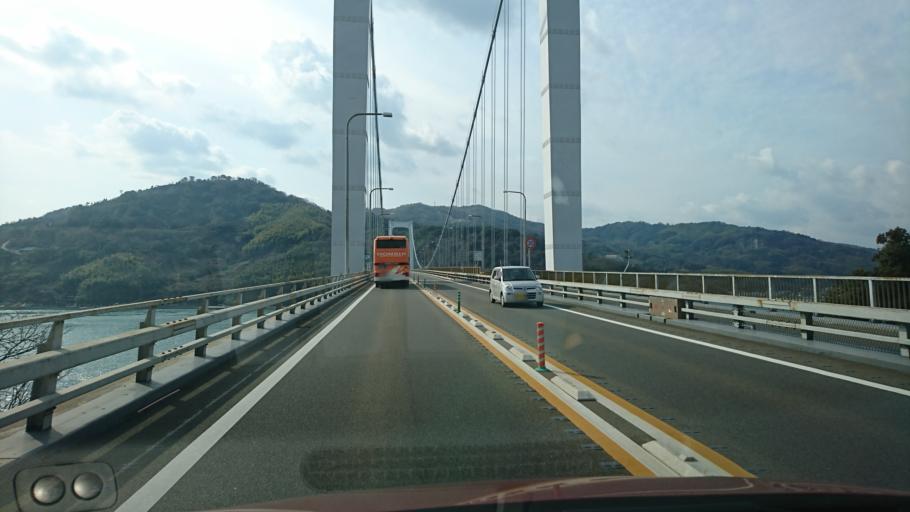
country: JP
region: Hiroshima
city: Innoshima
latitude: 34.1947
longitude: 133.0749
